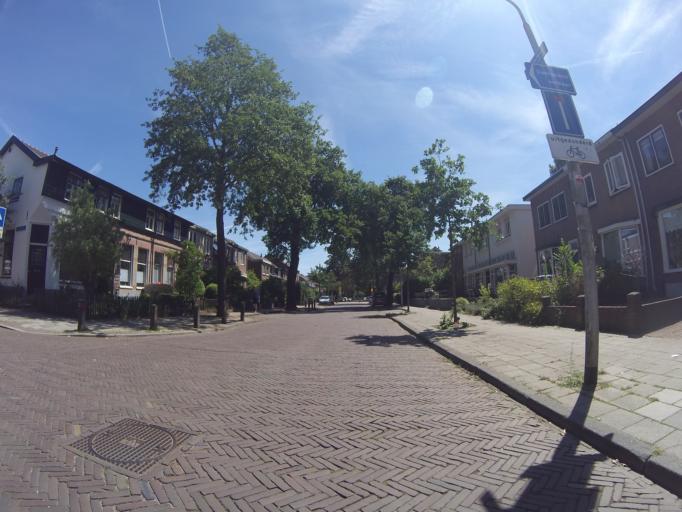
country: NL
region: Utrecht
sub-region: Gemeente Amersfoort
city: Amersfoort
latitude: 52.1557
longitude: 5.3734
